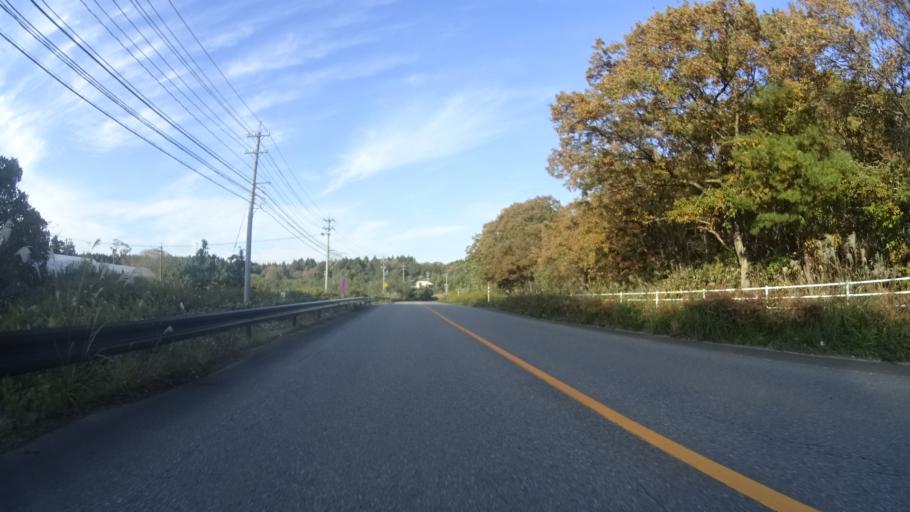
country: JP
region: Ishikawa
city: Hakui
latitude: 37.0545
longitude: 136.7764
